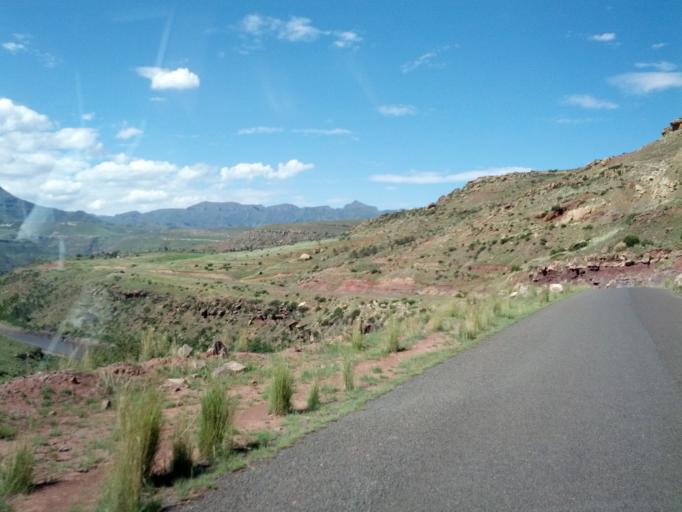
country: LS
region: Qacha's Nek
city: Qacha's Nek
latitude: -30.0717
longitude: 28.4682
